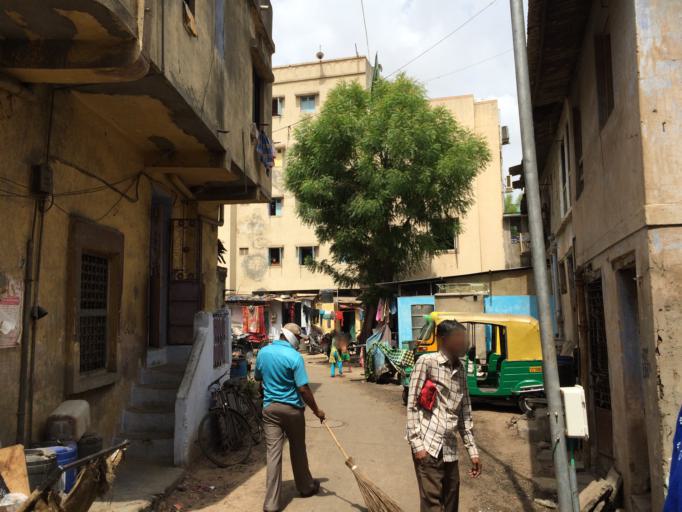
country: IN
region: Gujarat
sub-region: Ahmadabad
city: Ahmedabad
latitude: 23.0143
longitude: 72.5862
